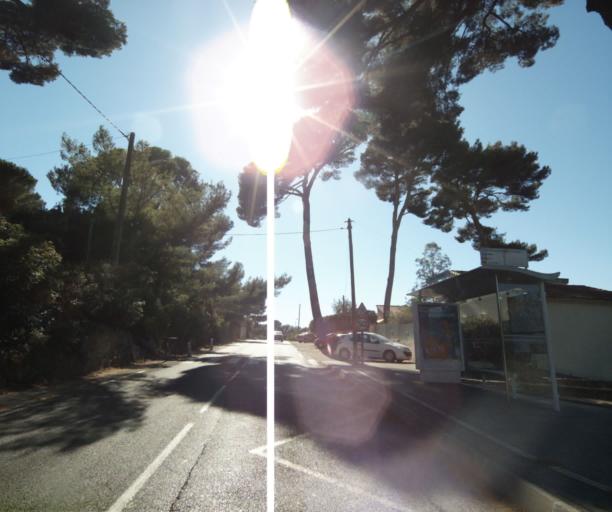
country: FR
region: Provence-Alpes-Cote d'Azur
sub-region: Departement du Var
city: La Garde
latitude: 43.1076
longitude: 5.9889
